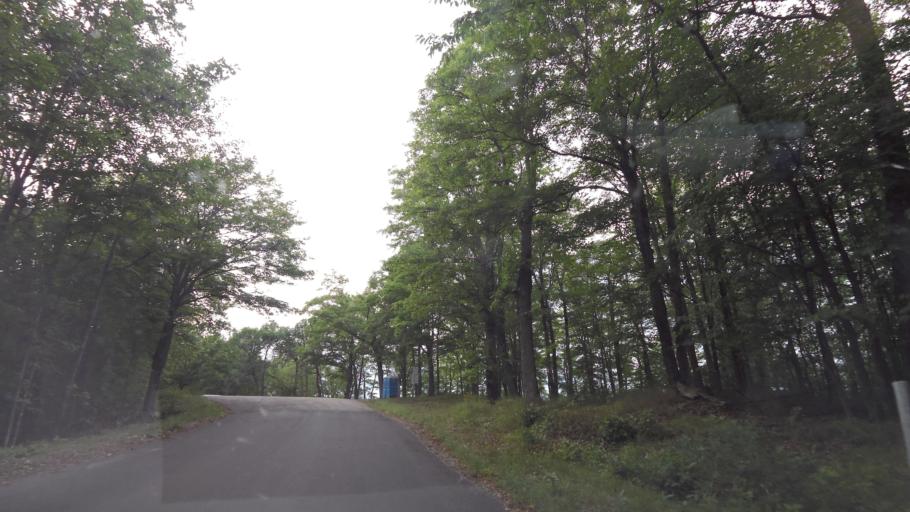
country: CA
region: Ontario
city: Bancroft
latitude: 45.0432
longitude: -78.5014
